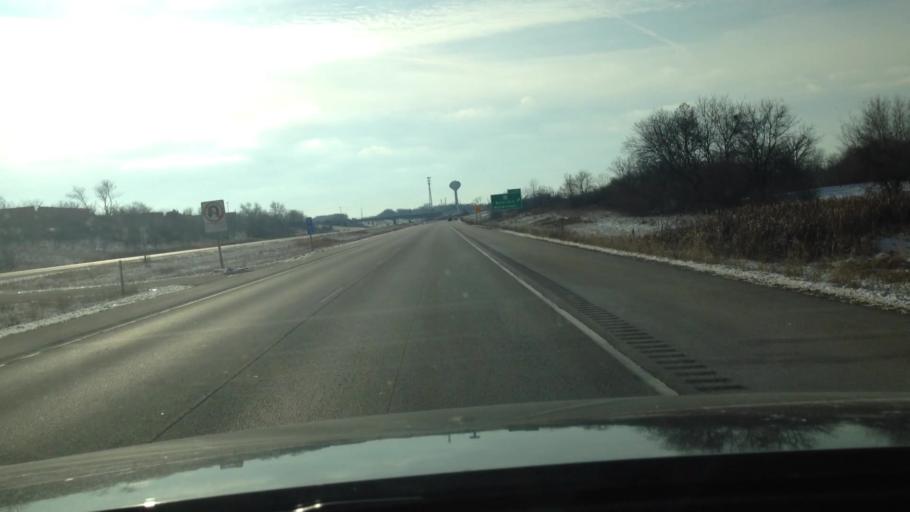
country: US
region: Wisconsin
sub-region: Waukesha County
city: Mukwonago
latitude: 42.8571
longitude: -88.3134
